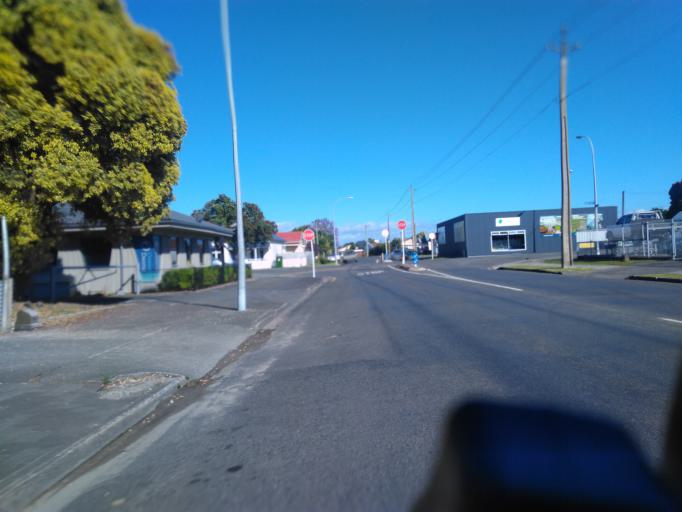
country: NZ
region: Gisborne
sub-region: Gisborne District
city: Gisborne
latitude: -38.6675
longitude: 178.0215
